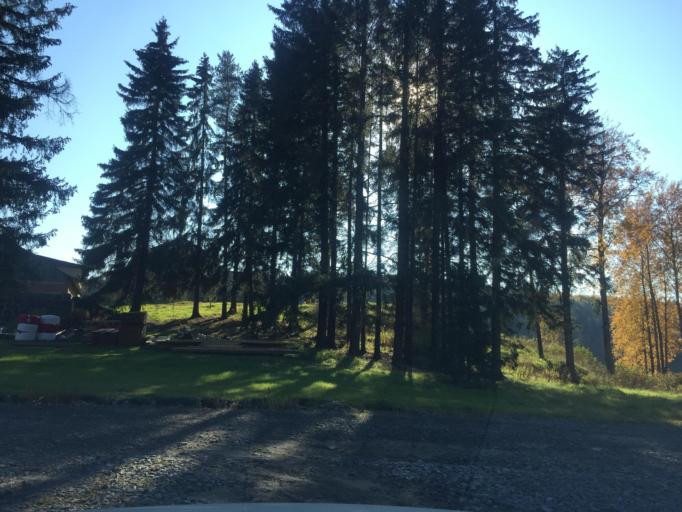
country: RU
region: Leningrad
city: Kuznechnoye
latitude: 61.2990
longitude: 29.9087
